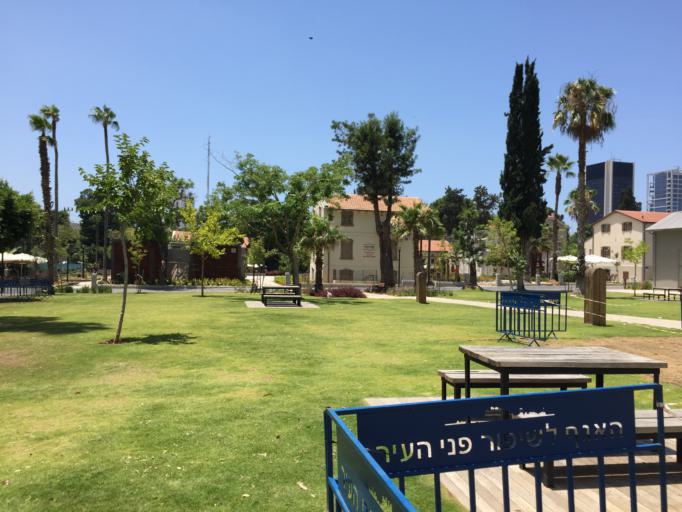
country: IL
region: Tel Aviv
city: Tel Aviv
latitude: 32.0720
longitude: 34.7877
